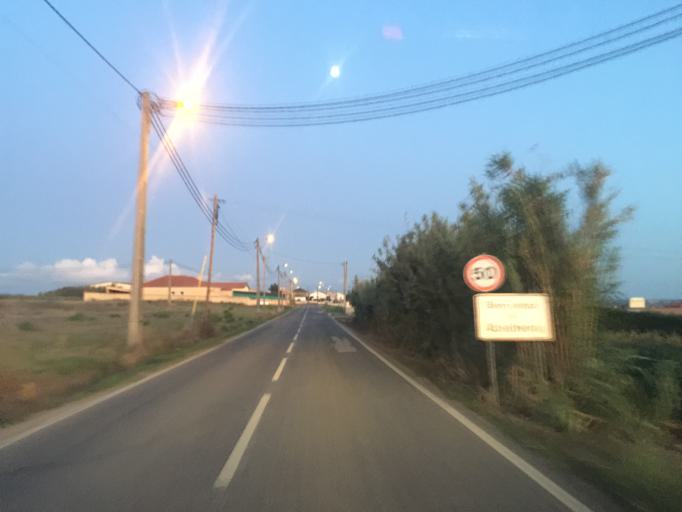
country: PT
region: Lisbon
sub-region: Lourinha
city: Lourinha
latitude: 39.2865
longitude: -9.3044
